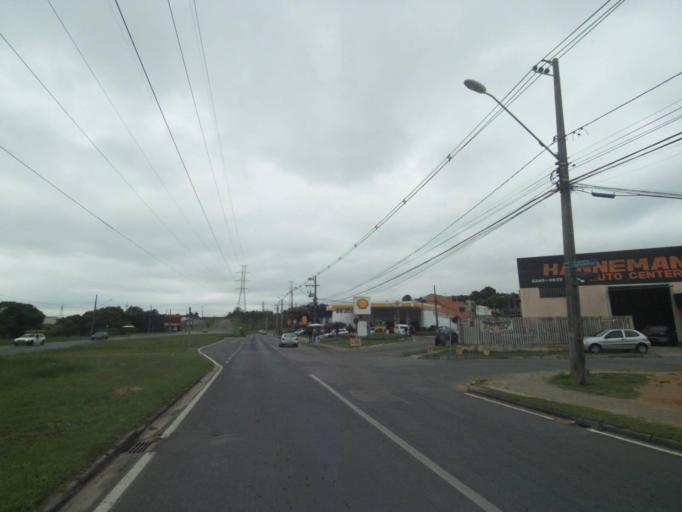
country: BR
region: Parana
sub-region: Araucaria
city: Araucaria
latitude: -25.5565
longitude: -49.3323
